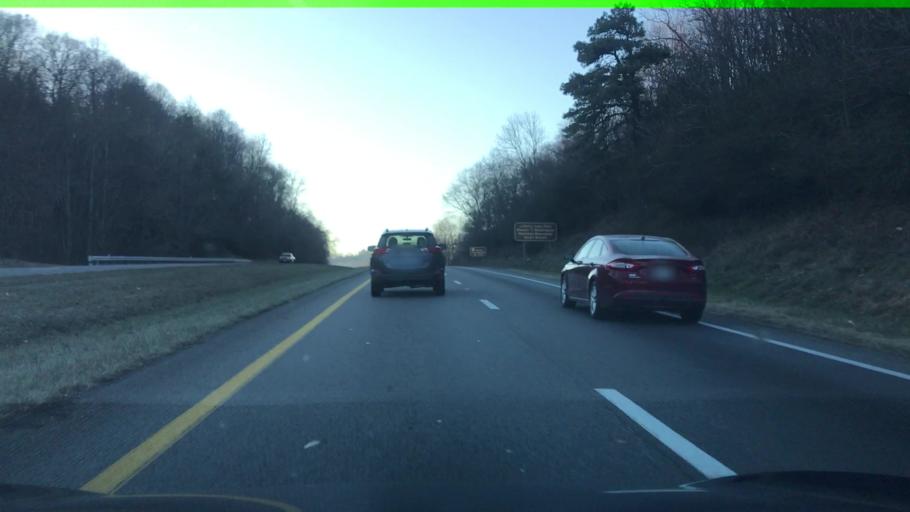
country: US
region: Virginia
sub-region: City of Bedford
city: Bedford
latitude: 37.3232
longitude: -79.5190
